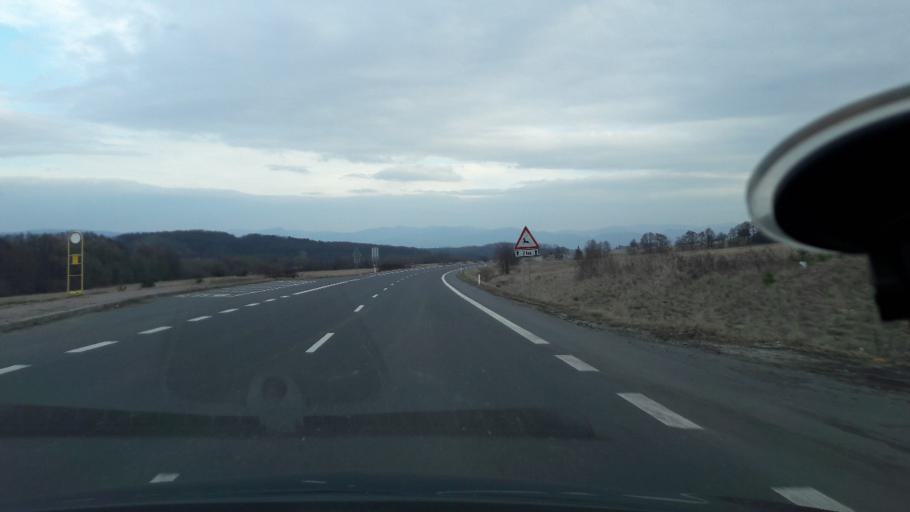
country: SK
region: Nitriansky
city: Handlova
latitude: 48.6444
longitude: 18.7678
